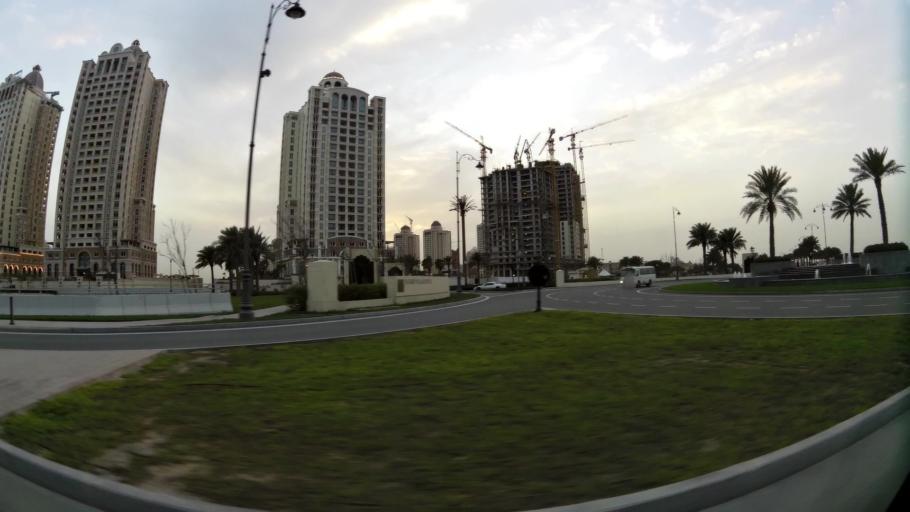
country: QA
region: Baladiyat ad Dawhah
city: Doha
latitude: 25.3695
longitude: 51.5621
